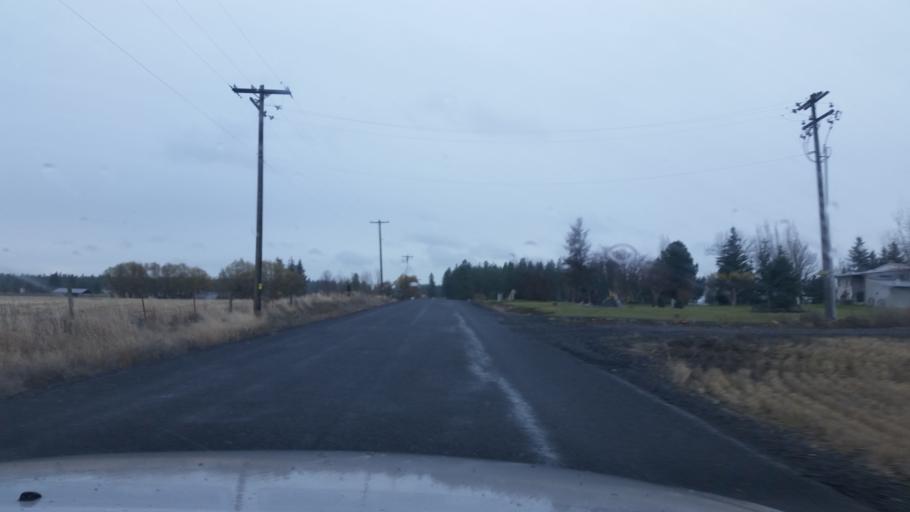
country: US
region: Washington
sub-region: Spokane County
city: Medical Lake
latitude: 47.6144
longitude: -117.7426
